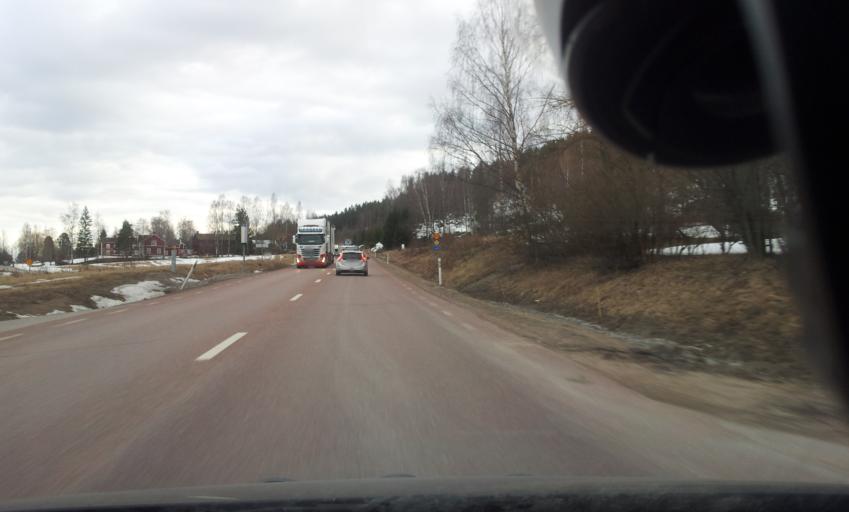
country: SE
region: Gaevleborg
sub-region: Ljusdals Kommun
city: Jaervsoe
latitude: 61.7474
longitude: 16.1595
